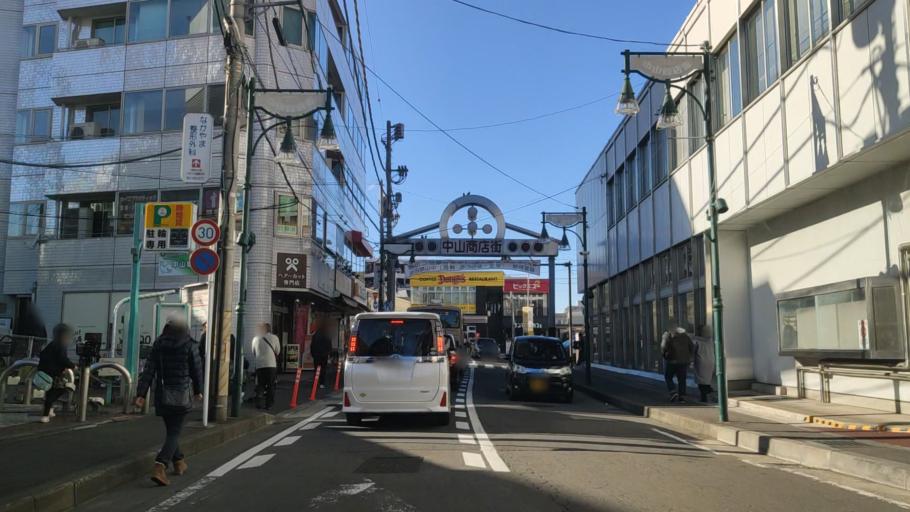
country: JP
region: Tokyo
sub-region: Machida-shi
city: Machida
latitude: 35.5139
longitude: 139.5402
